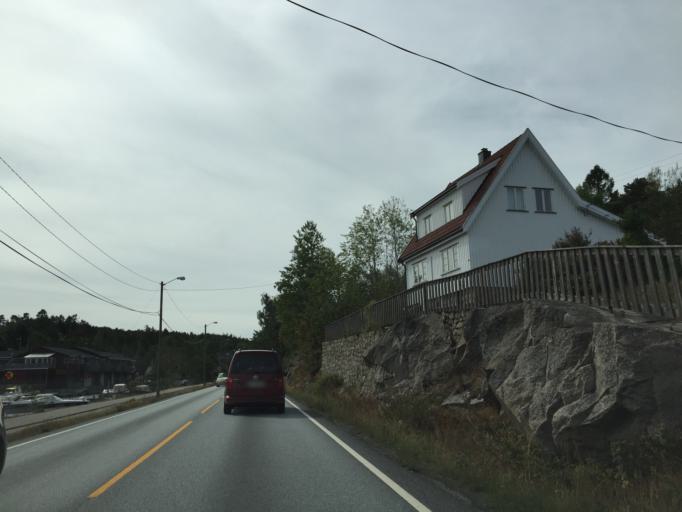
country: NO
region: Ostfold
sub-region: Fredrikstad
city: Fredrikstad
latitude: 59.1127
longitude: 10.9117
